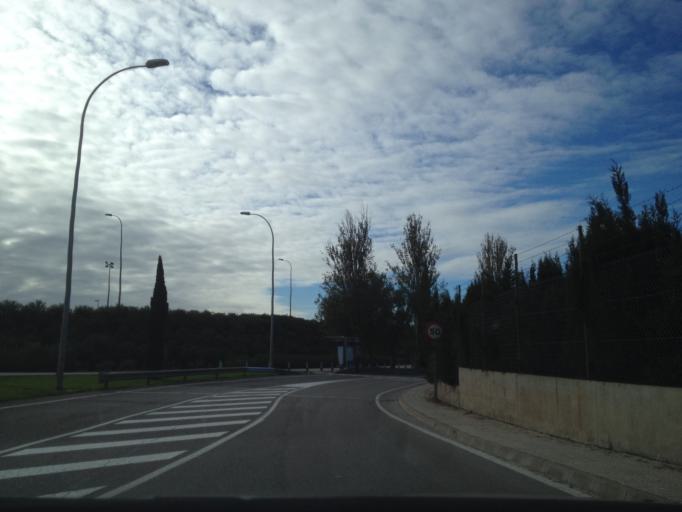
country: ES
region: Balearic Islands
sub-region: Illes Balears
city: s'Arenal
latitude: 39.5474
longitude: 2.7245
